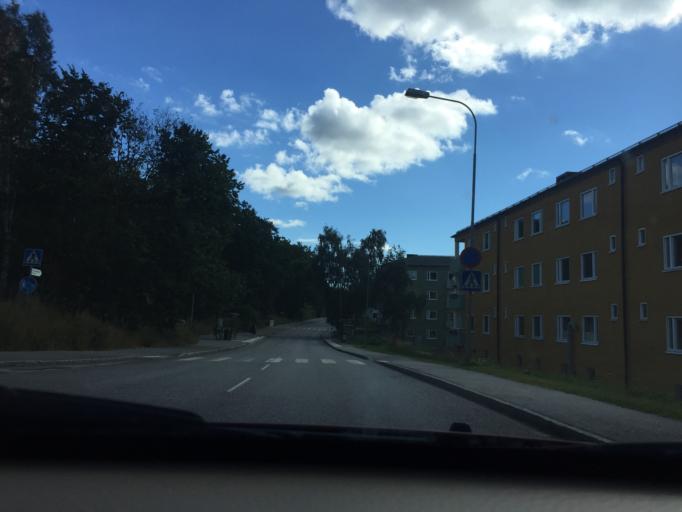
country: SE
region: Stockholm
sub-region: Nacka Kommun
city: Nacka
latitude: 59.3033
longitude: 18.1229
